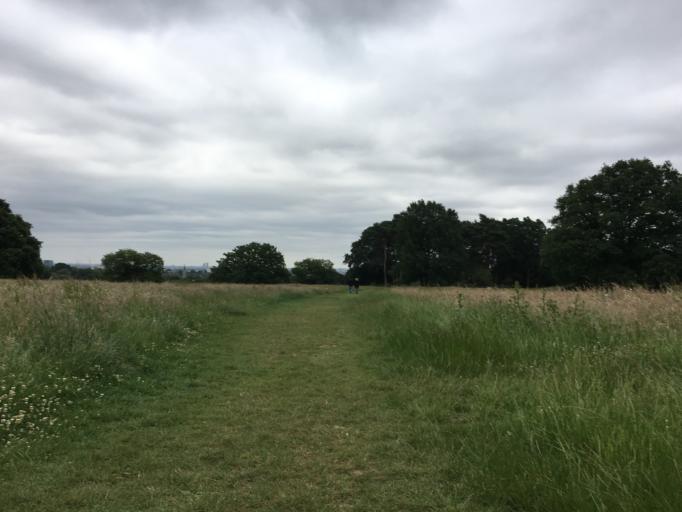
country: GB
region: England
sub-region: Greater London
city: Belsize Park
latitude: 51.5638
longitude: -0.1655
